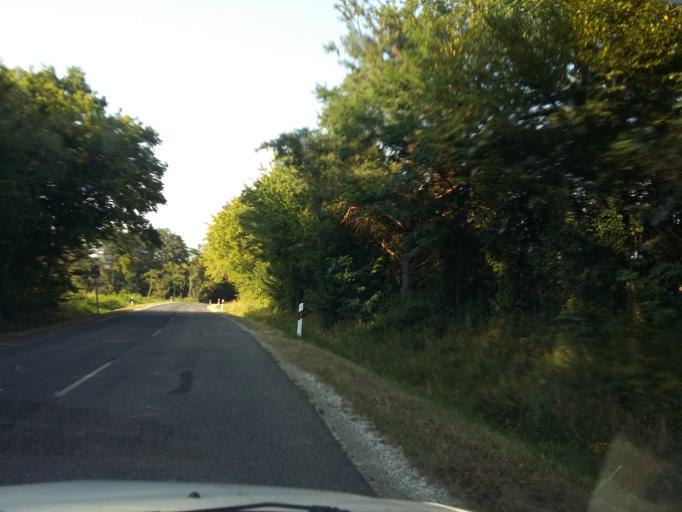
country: SI
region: Hodos-Hodos
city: Hodos
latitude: 46.8336
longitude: 16.4120
